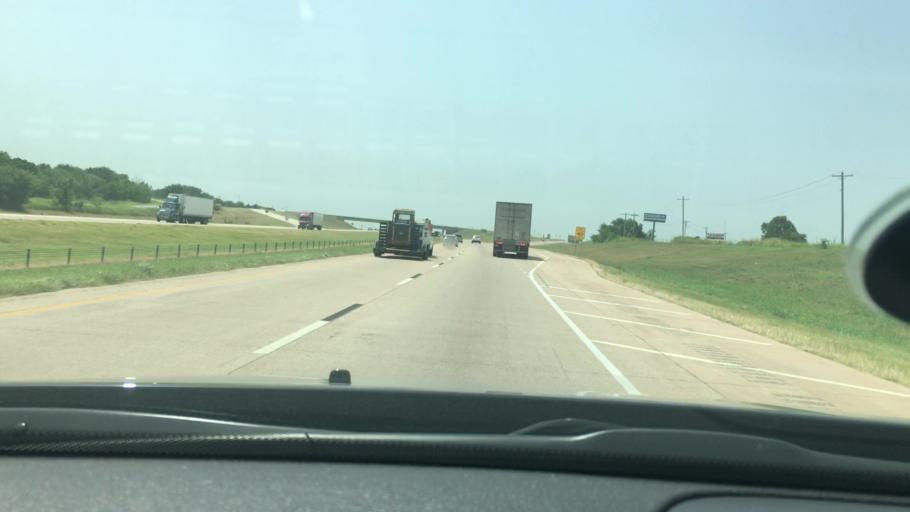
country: US
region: Oklahoma
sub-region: Garvin County
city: Pauls Valley
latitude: 34.7109
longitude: -97.2486
